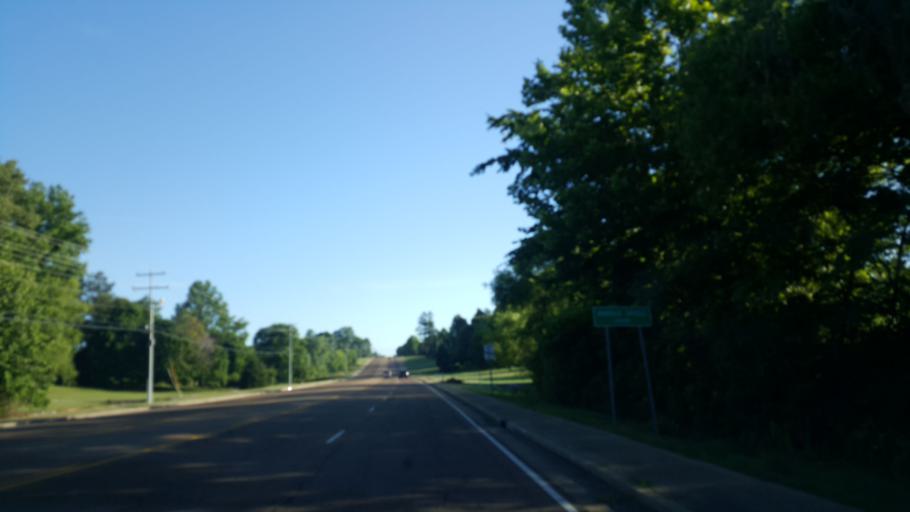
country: US
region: Tennessee
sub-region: Henderson County
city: Lexington
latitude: 35.6691
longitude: -88.3843
